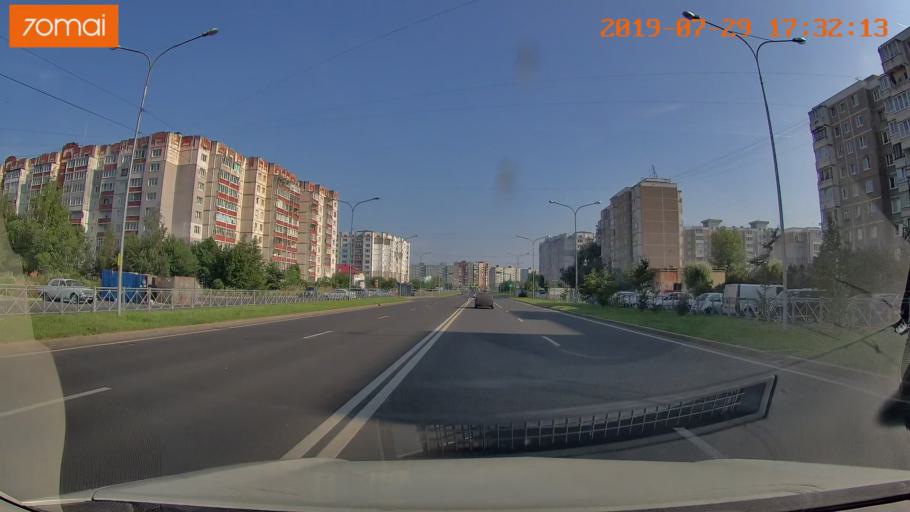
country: RU
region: Kaliningrad
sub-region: Gorod Kaliningrad
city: Kaliningrad
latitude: 54.7445
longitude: 20.4914
